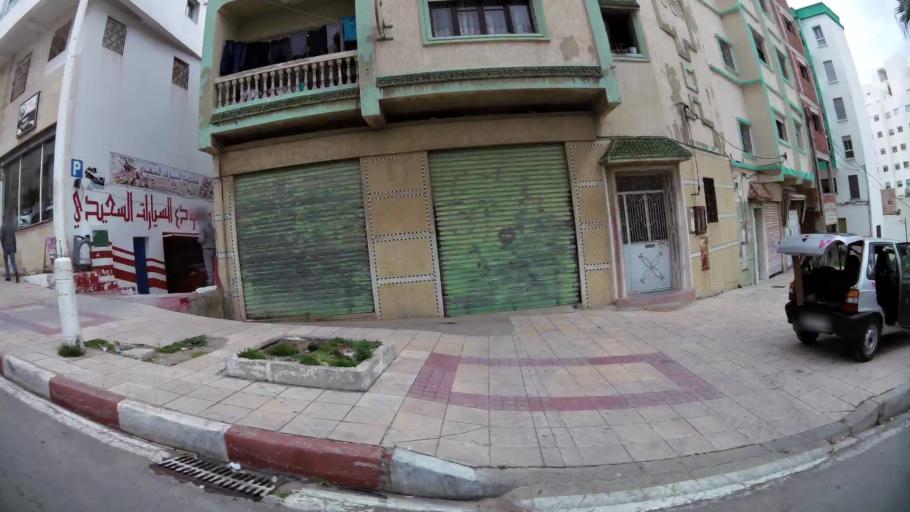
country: MA
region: Tanger-Tetouan
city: Tetouan
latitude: 35.5664
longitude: -5.3809
